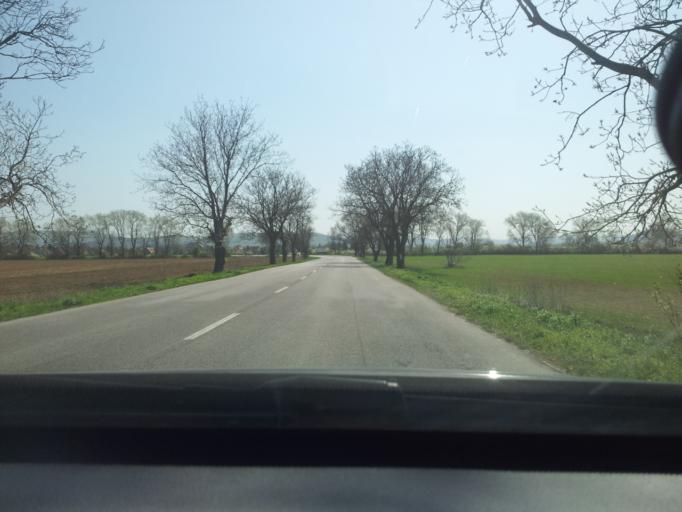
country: SK
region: Nitriansky
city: Banovce nad Bebravou
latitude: 48.6149
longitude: 18.2560
